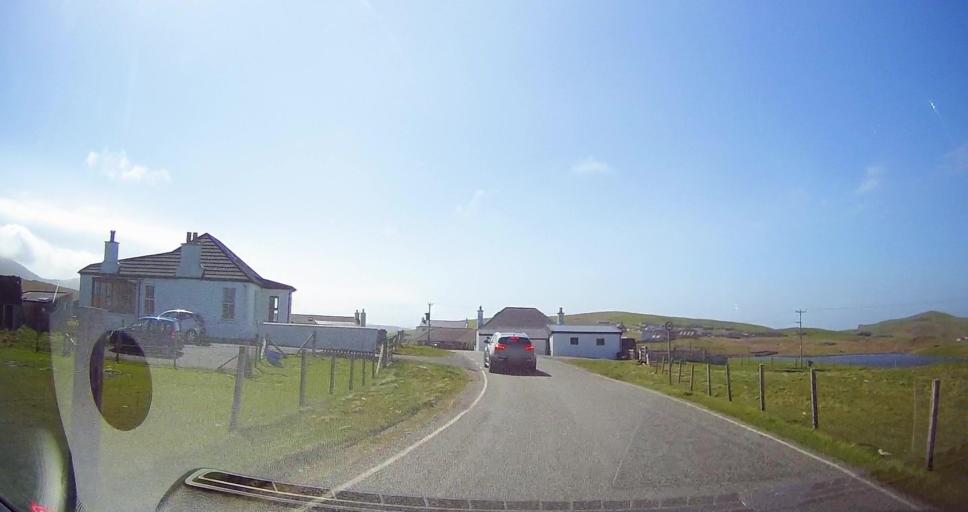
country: GB
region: Scotland
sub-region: Shetland Islands
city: Sandwick
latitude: 60.0849
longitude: -1.3320
